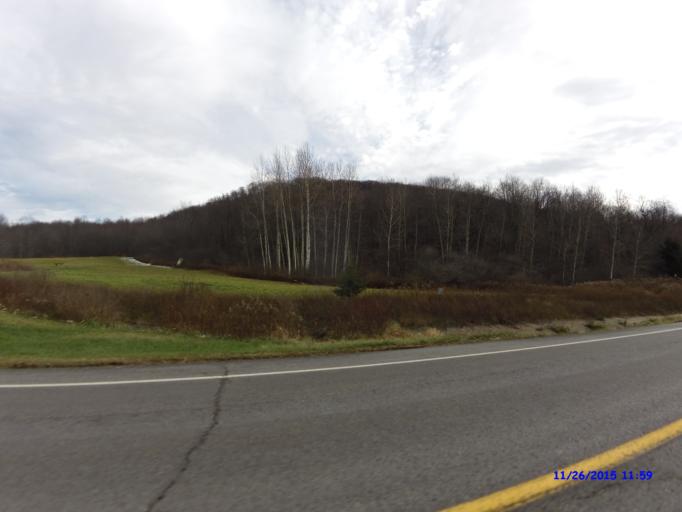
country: US
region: New York
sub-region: Cattaraugus County
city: Franklinville
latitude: 42.2995
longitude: -78.4568
